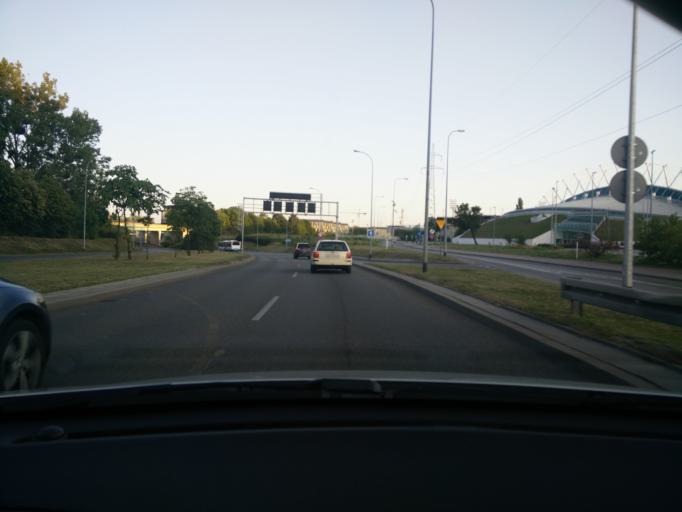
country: PL
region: Pomeranian Voivodeship
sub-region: Gdynia
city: Gdynia
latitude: 54.5009
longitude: 18.5326
